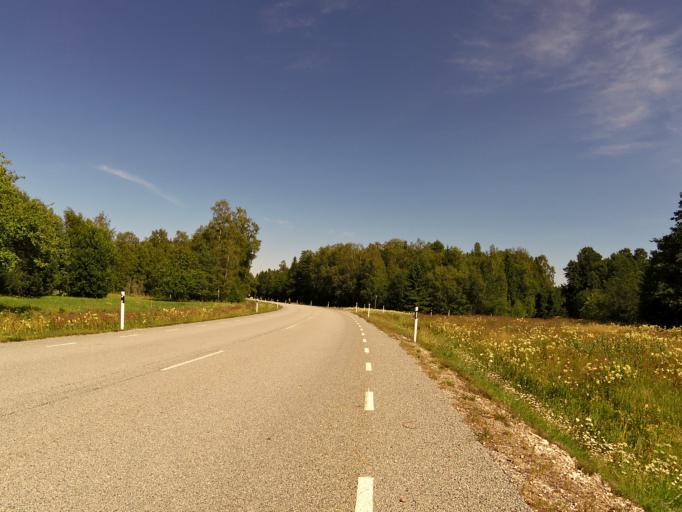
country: EE
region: Hiiumaa
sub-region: Kaerdla linn
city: Kardla
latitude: 59.0022
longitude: 22.5833
